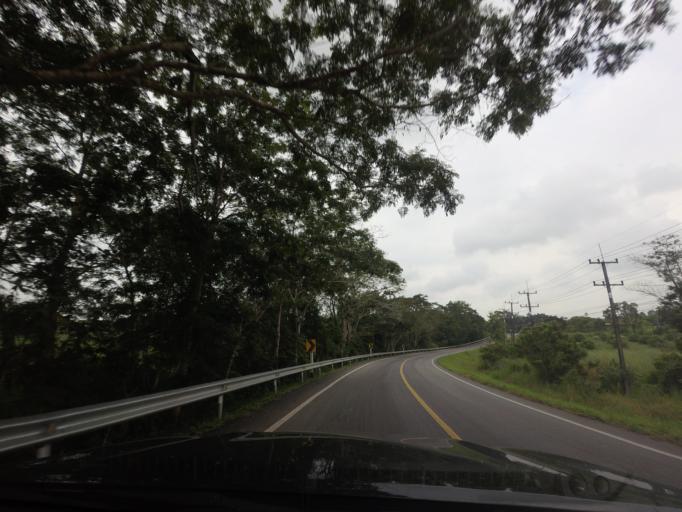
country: TH
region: Nong Khai
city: Si Chiang Mai
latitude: 17.9542
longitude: 102.4926
